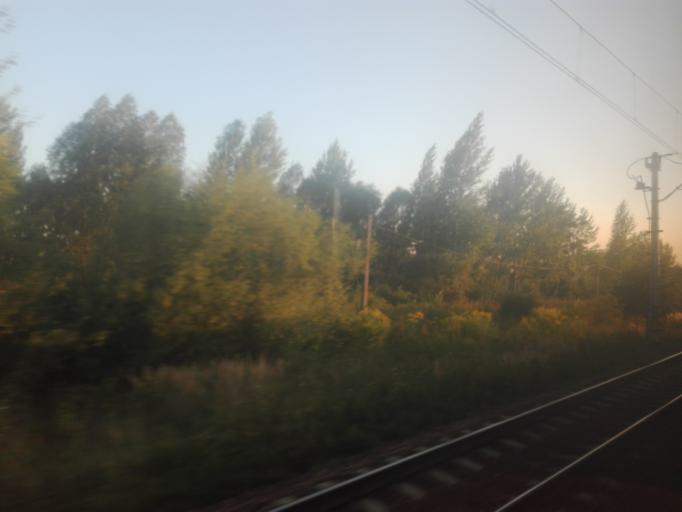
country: PL
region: Masovian Voivodeship
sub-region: Powiat warszawski zachodni
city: Bieniewice
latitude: 52.1863
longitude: 20.5886
